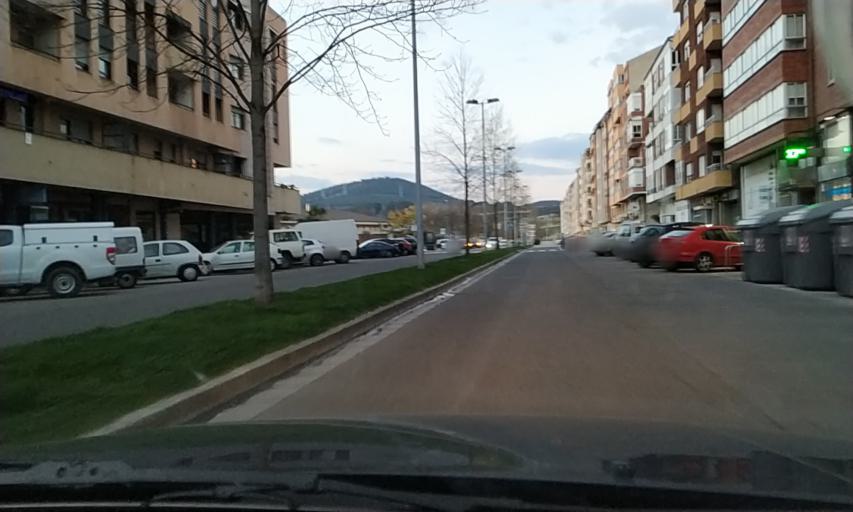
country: ES
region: Castille and Leon
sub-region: Provincia de Leon
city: Ponferrada
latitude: 42.5493
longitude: -6.5897
